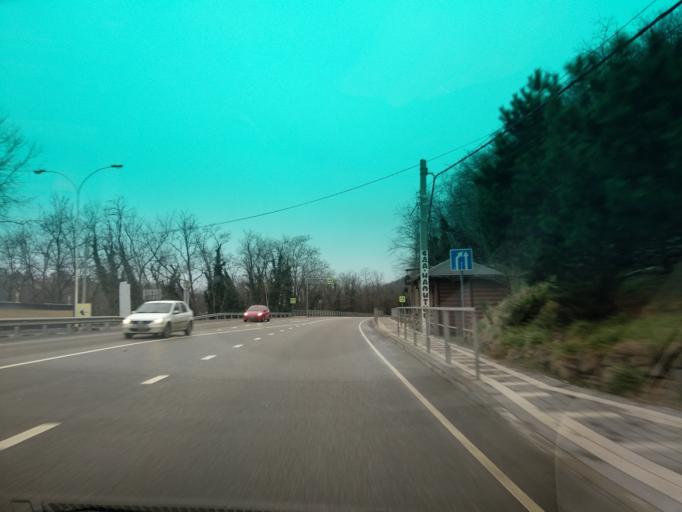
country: RU
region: Krasnodarskiy
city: Tuapse
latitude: 44.1066
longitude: 39.0746
